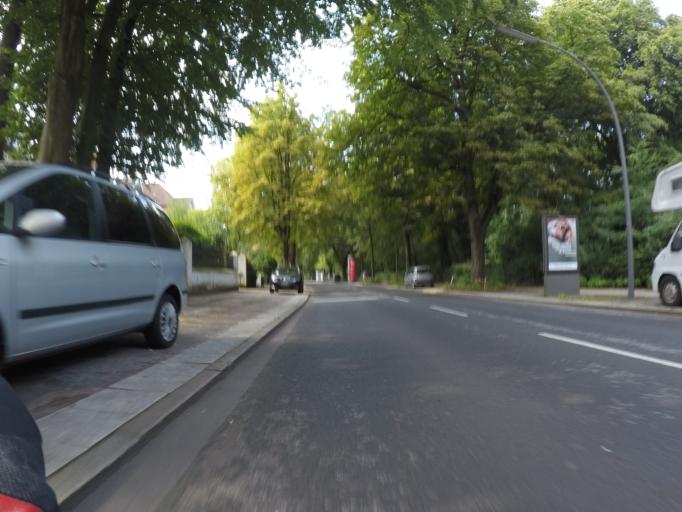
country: DE
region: Hamburg
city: Ohlsdorf
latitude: 53.6311
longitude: 10.0397
